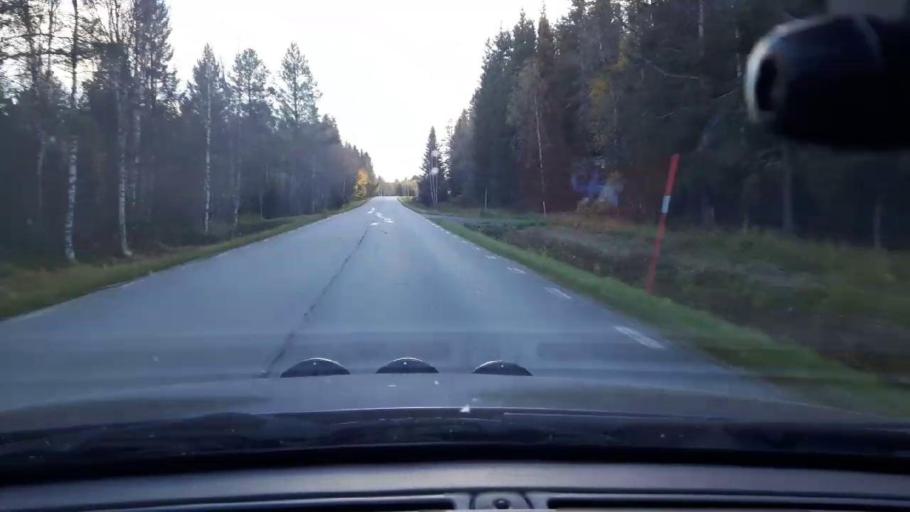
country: SE
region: Jaemtland
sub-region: Bergs Kommun
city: Hoverberg
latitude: 63.0280
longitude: 14.3448
